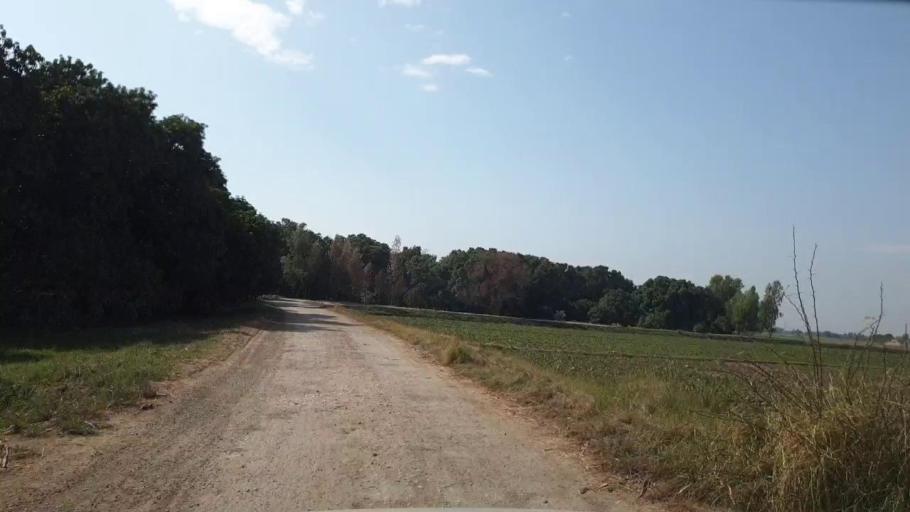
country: PK
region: Sindh
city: Matiari
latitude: 25.5593
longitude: 68.4637
